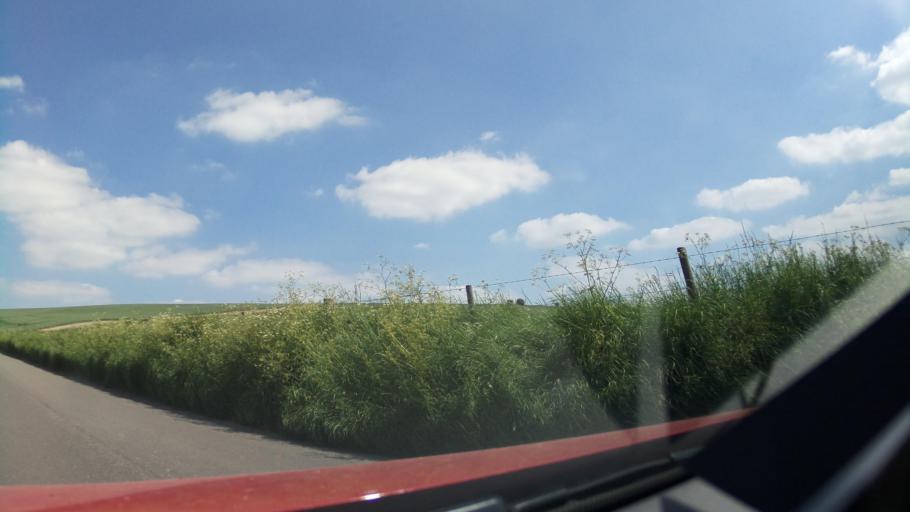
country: GB
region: England
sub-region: Wiltshire
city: Woodborough
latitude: 51.3594
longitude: -1.8390
